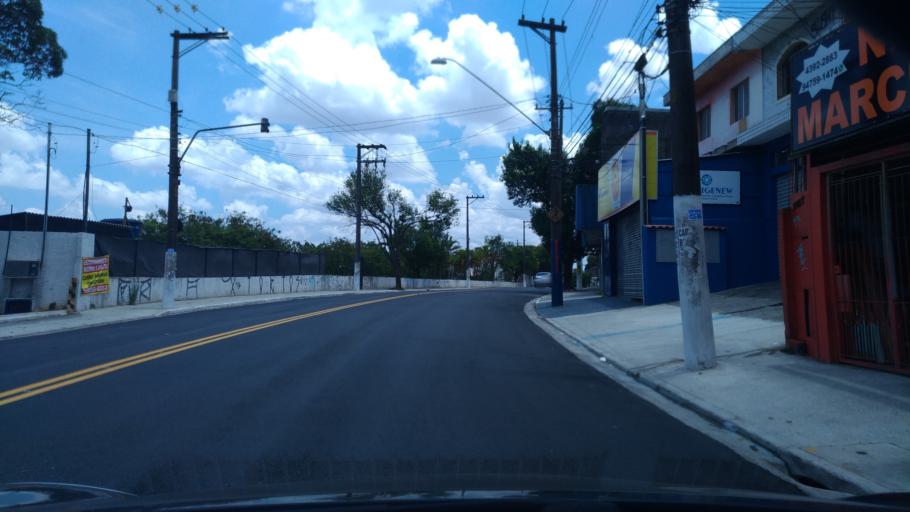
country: BR
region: Sao Paulo
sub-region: Sao Bernardo Do Campo
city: Sao Bernardo do Campo
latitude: -23.7011
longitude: -46.5878
